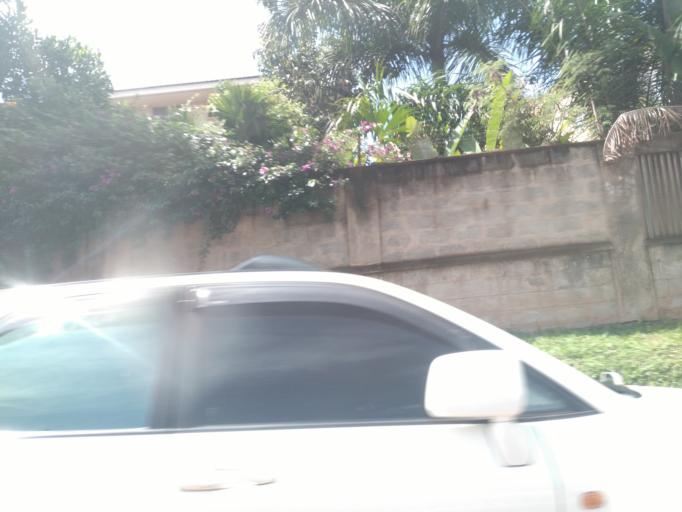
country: UG
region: Central Region
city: Kampala Central Division
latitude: 0.3306
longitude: 32.5786
